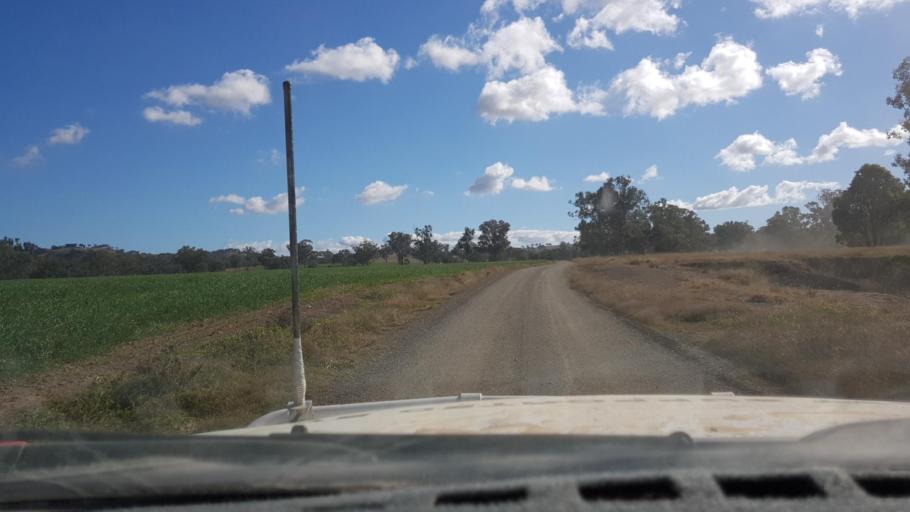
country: AU
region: New South Wales
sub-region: Narrabri
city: Blair Athol
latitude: -30.5783
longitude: 150.4723
